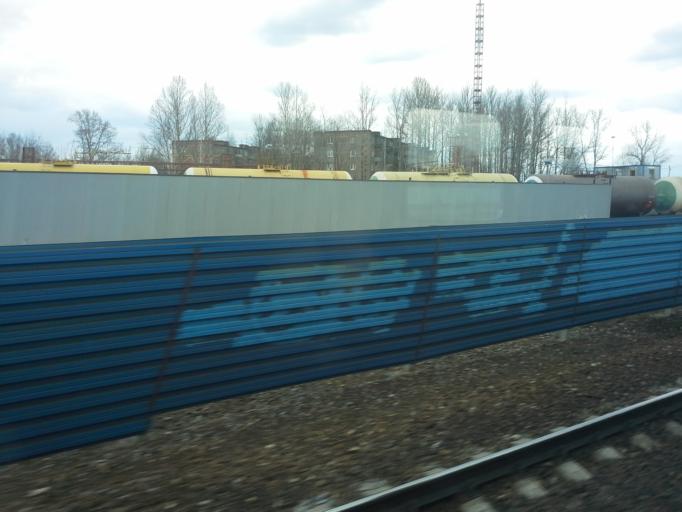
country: RU
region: Moskovskaya
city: Sofrino
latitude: 56.1461
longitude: 37.9370
